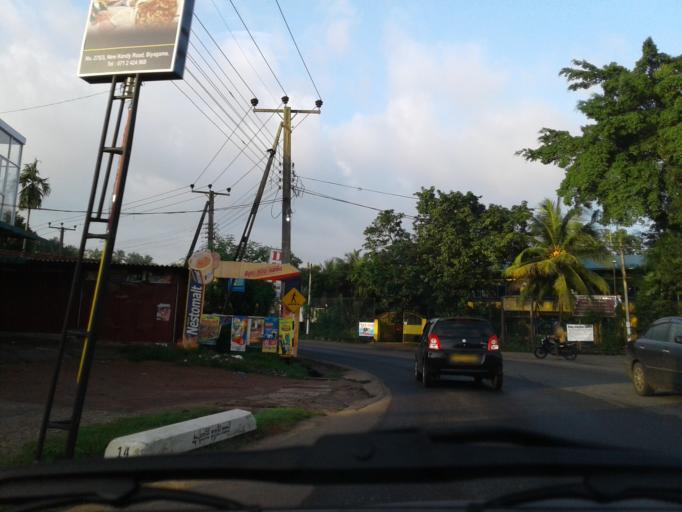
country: LK
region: Western
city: Mulleriyawa
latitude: 6.9492
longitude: 79.9915
